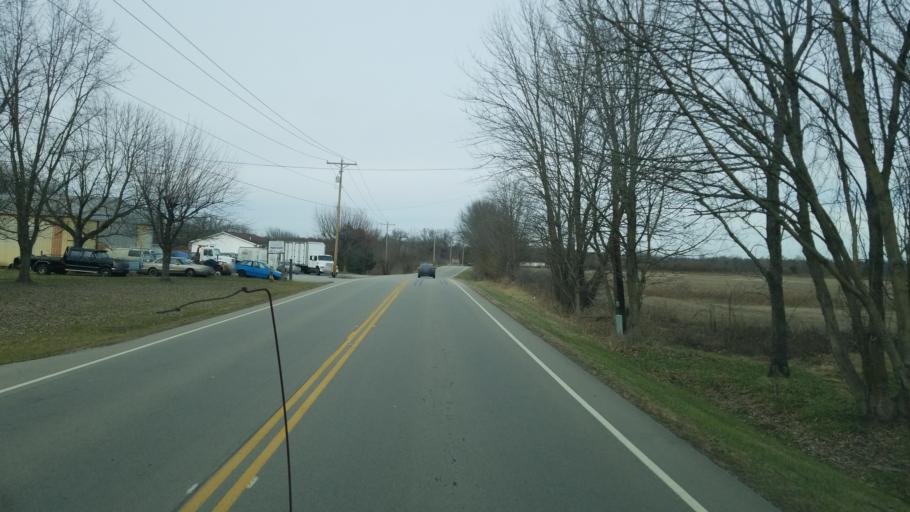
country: US
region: Ohio
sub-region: Adams County
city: Winchester
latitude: 39.0313
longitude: -83.7049
